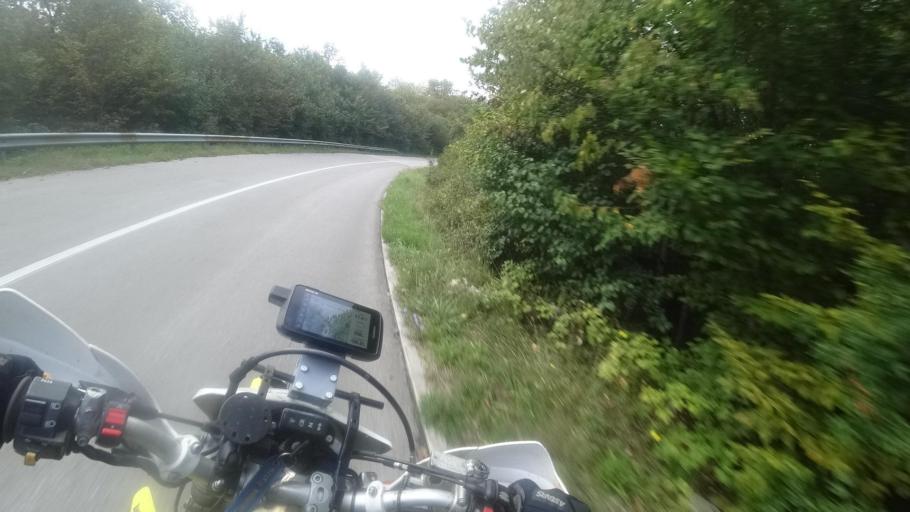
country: BA
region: Federation of Bosnia and Herzegovina
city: Bosanska Krupa
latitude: 44.8030
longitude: 16.2312
